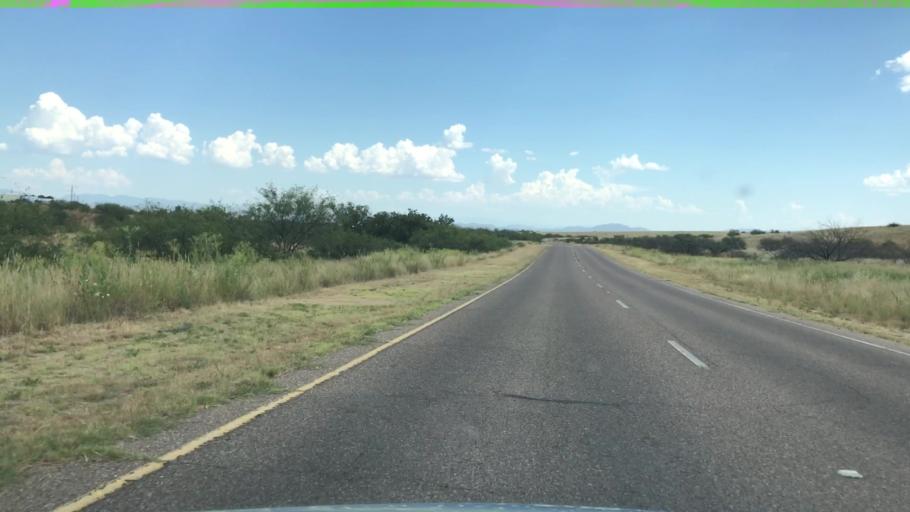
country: US
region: Arizona
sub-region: Cochise County
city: Sierra Vista
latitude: 31.5433
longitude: -110.3324
